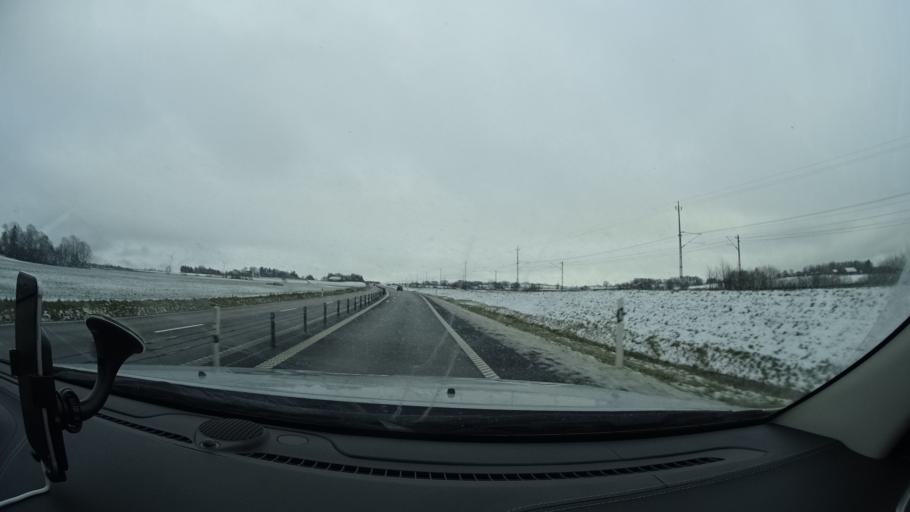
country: SE
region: OEstergoetland
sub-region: Motala Kommun
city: Stenstorp
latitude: 58.4940
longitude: 15.0262
